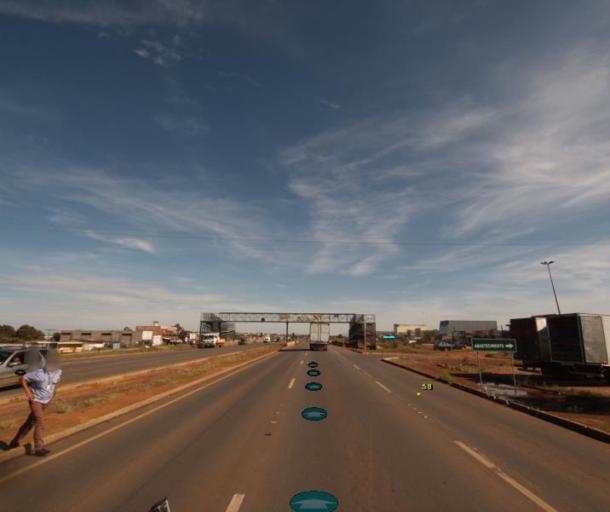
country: BR
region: Federal District
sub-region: Brasilia
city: Brasilia
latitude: -15.7519
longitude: -48.2600
